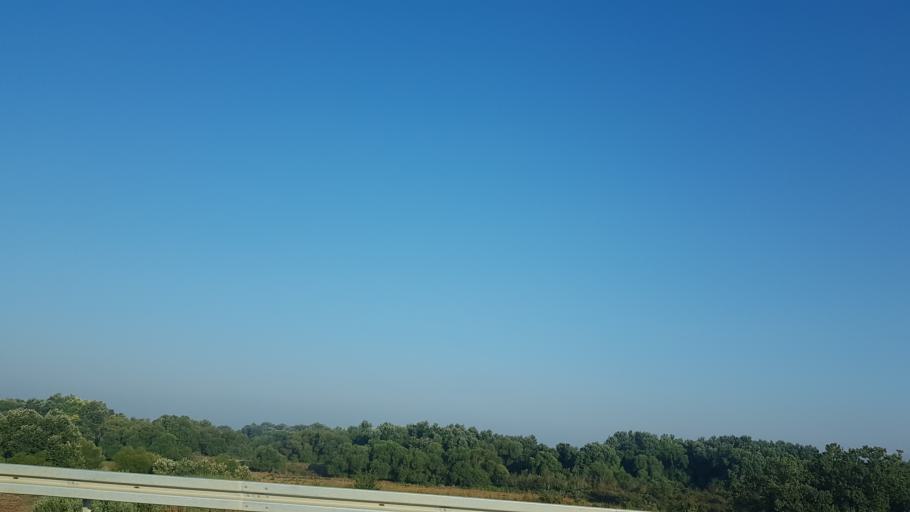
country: TR
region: Bursa
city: Karacabey
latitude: 40.1664
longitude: 28.3196
